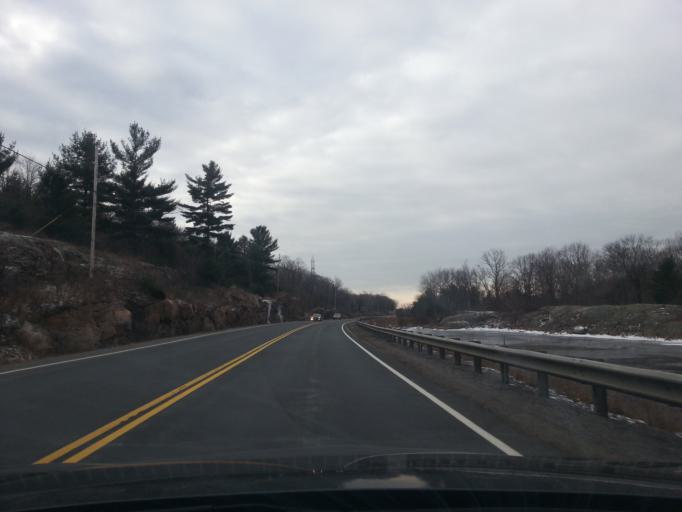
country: CA
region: Ontario
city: Greater Napanee
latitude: 44.6029
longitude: -77.1855
